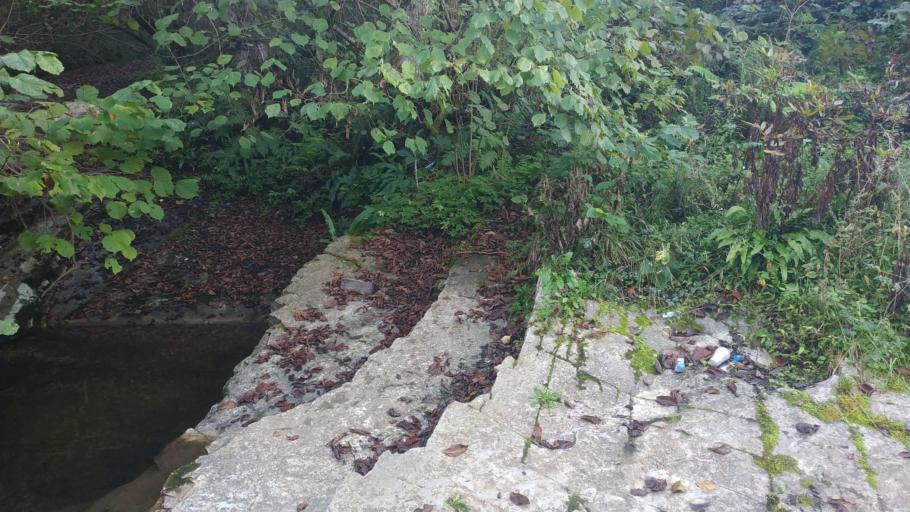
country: RU
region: Krasnodarskiy
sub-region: Sochi City
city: Lazarevskoye
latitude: 44.0010
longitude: 39.3674
